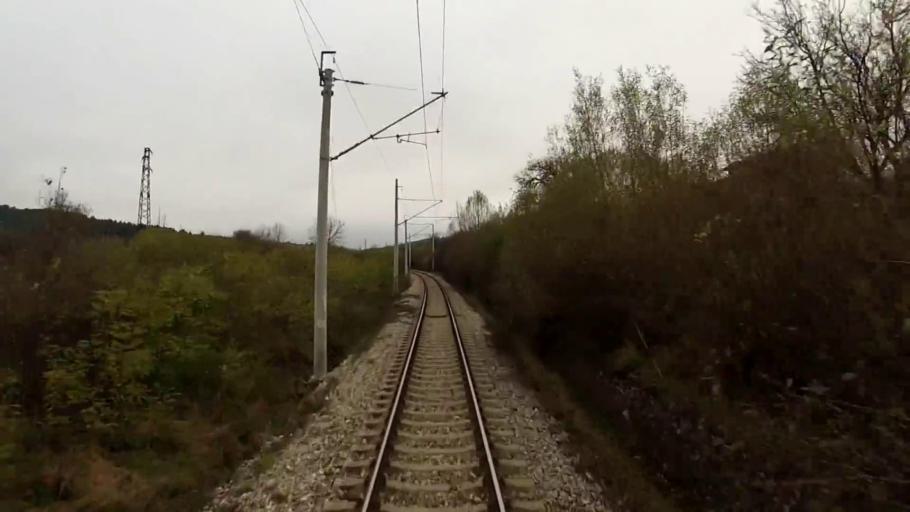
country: BG
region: Sofiya
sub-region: Obshtina Dragoman
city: Dragoman
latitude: 42.9365
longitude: 22.9033
